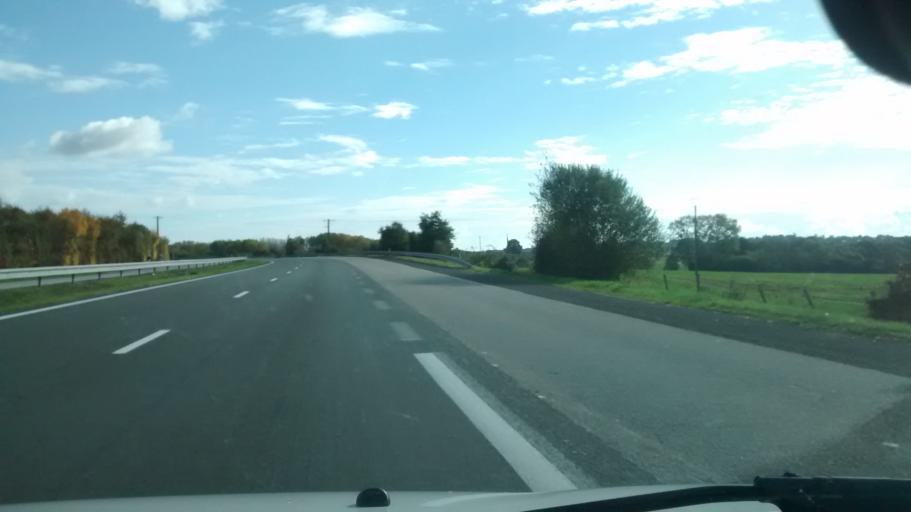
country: FR
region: Pays de la Loire
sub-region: Departement de Maine-et-Loire
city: Pouance
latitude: 47.7590
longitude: -1.1903
